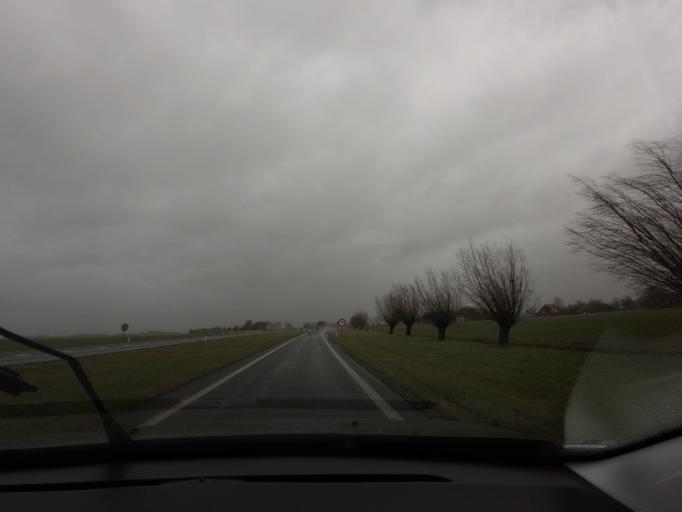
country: NL
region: Friesland
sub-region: Sudwest Fryslan
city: Bolsward
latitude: 53.0915
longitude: 5.5319
